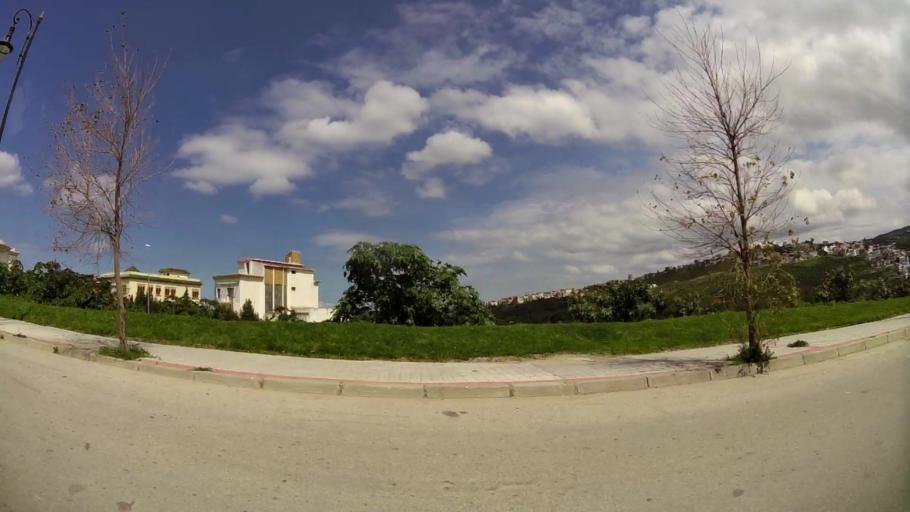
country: MA
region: Tanger-Tetouan
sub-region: Tanger-Assilah
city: Tangier
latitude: 35.7715
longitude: -5.7653
